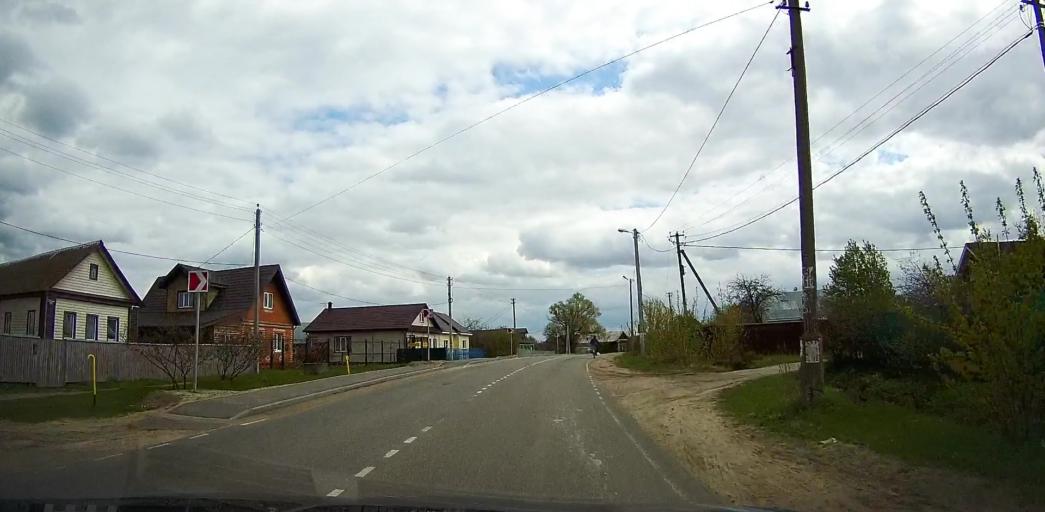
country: RU
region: Moskovskaya
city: Imeni Tsyurupy
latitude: 55.4976
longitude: 38.6510
